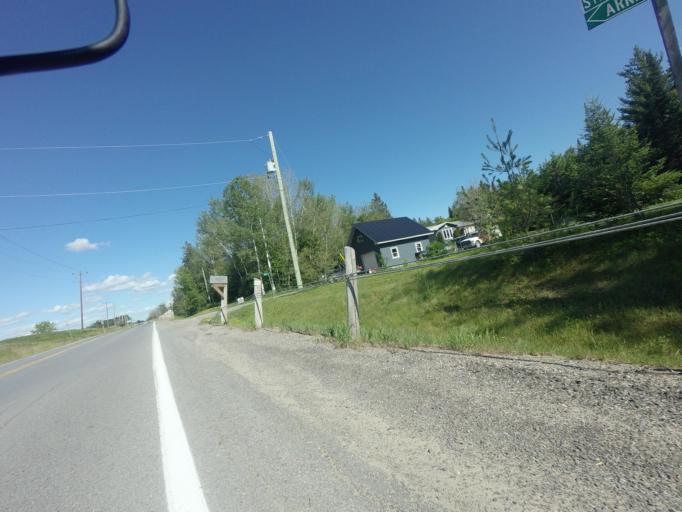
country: CA
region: Ontario
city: Arnprior
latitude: 45.4106
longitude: -76.4458
